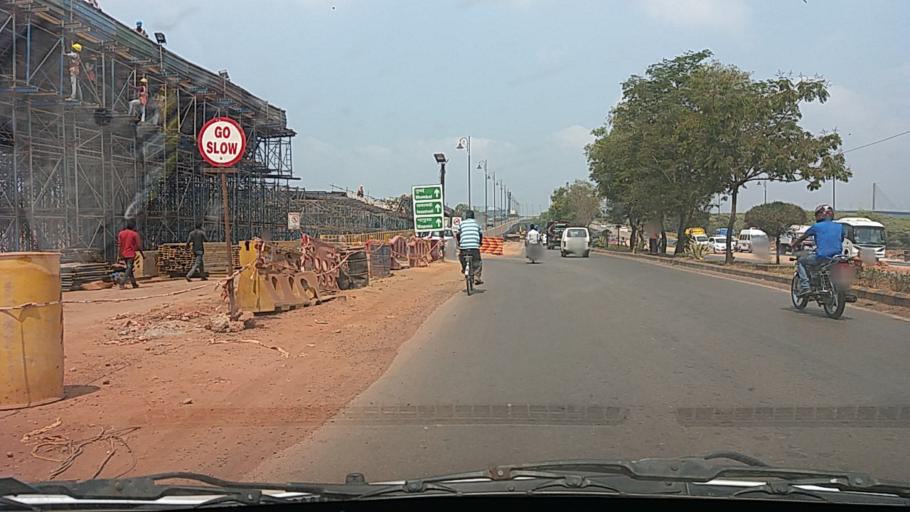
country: IN
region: Goa
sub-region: North Goa
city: Panaji
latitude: 15.4923
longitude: 73.8424
